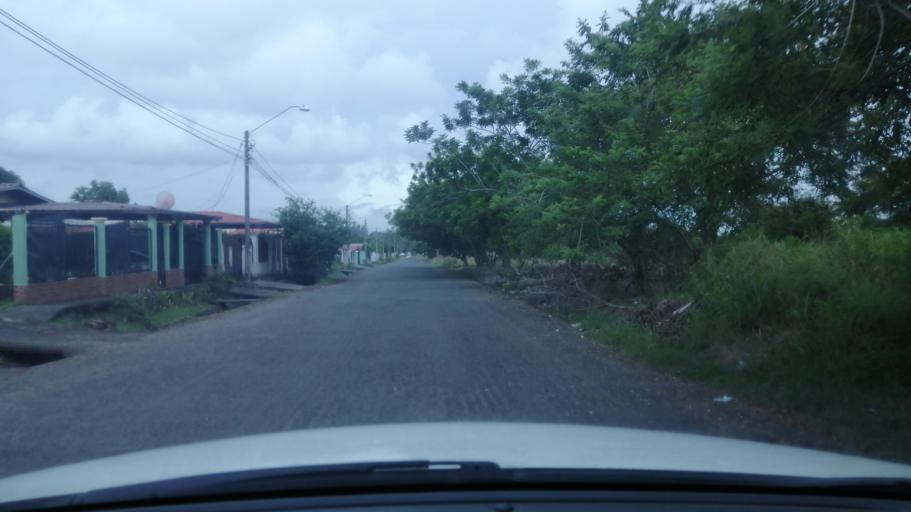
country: PA
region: Chiriqui
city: David
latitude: 8.4045
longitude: -82.4506
